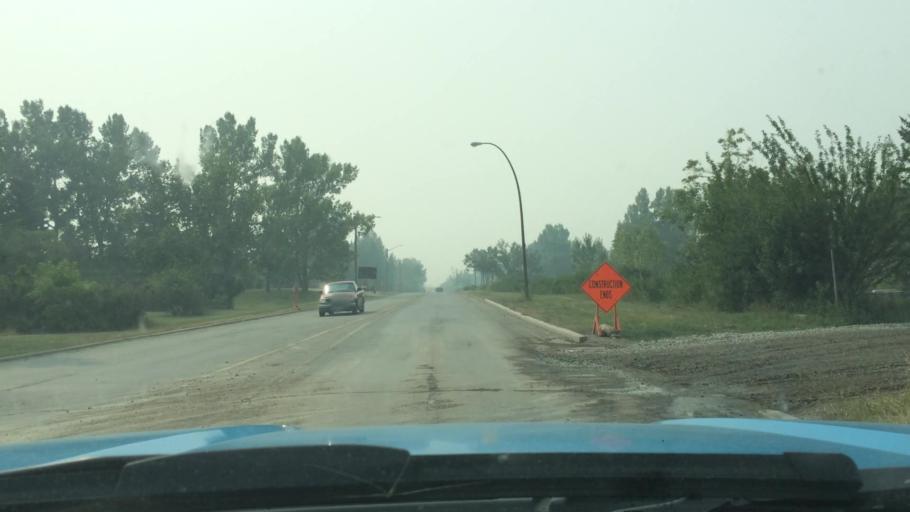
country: CA
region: Alberta
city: Calgary
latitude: 50.9485
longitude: -114.0948
